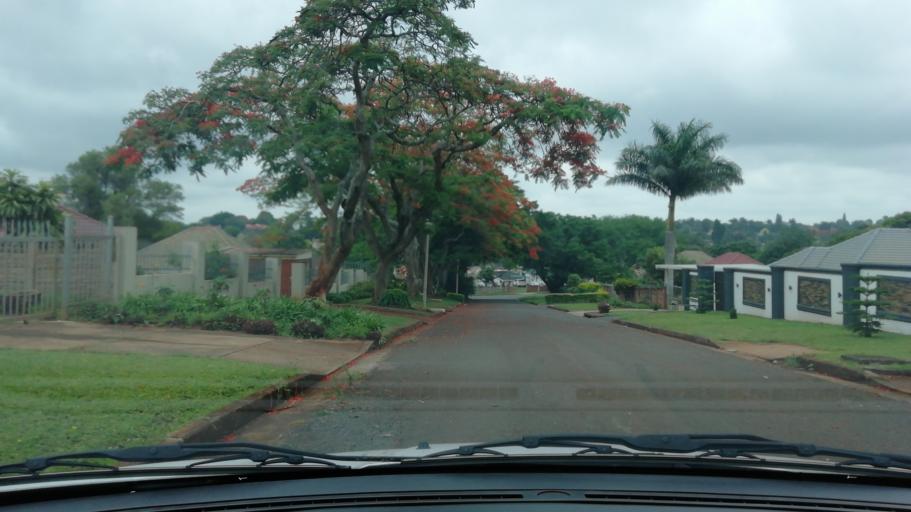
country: ZA
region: KwaZulu-Natal
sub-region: uThungulu District Municipality
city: Empangeni
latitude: -28.7618
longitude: 31.9031
